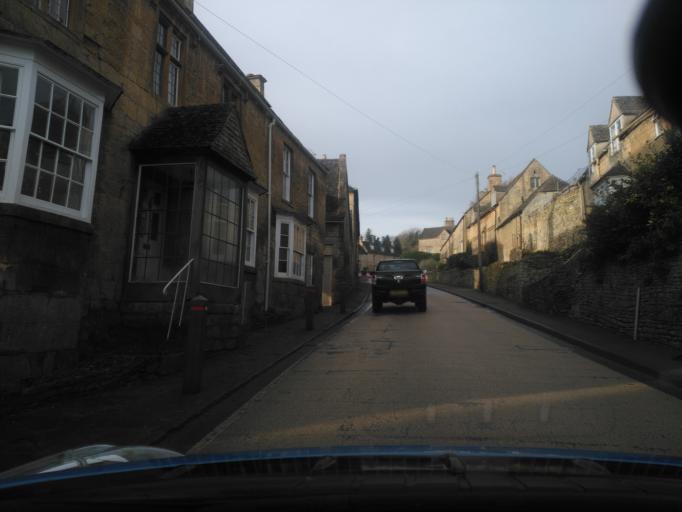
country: GB
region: England
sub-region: Gloucestershire
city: Moreton in Marsh
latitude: 51.9911
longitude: -1.7463
